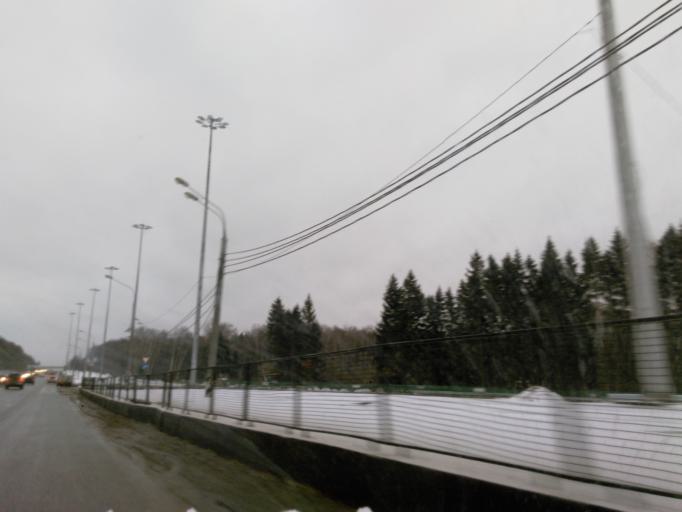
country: RU
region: Moskovskaya
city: Mendeleyevo
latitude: 56.0138
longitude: 37.2088
